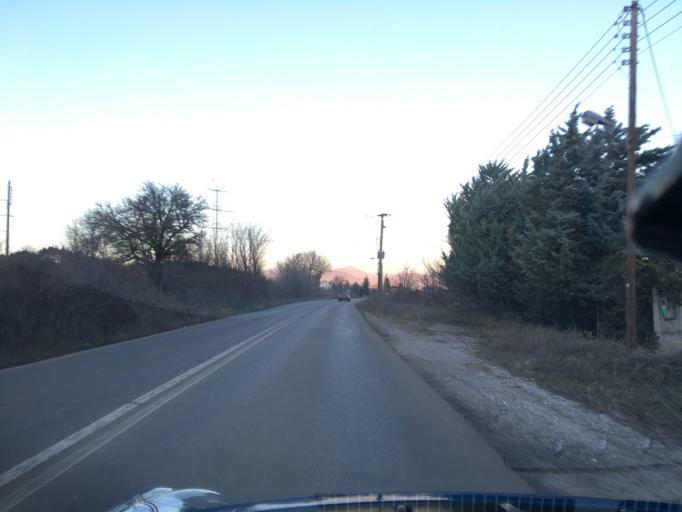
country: GR
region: West Macedonia
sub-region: Nomos Kozanis
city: Kozani
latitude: 40.2614
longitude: 21.7626
